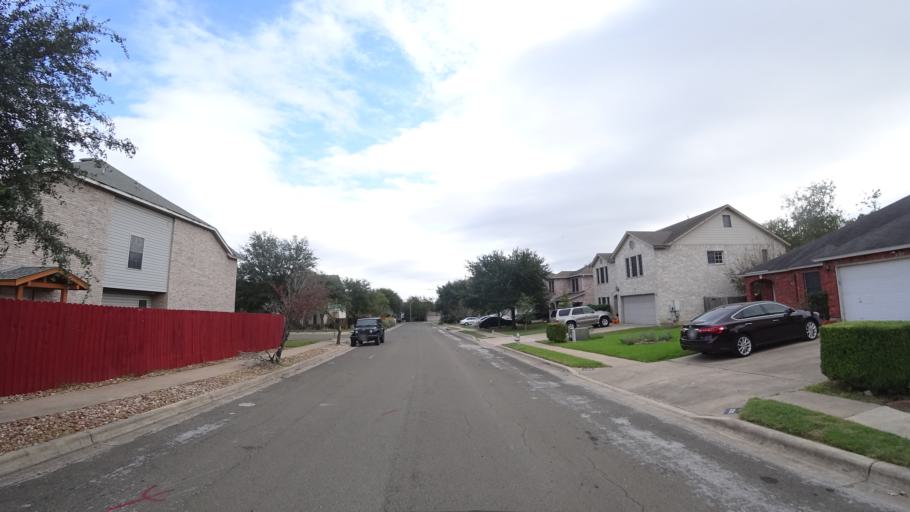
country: US
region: Texas
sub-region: Travis County
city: Manchaca
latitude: 30.1557
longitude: -97.8412
